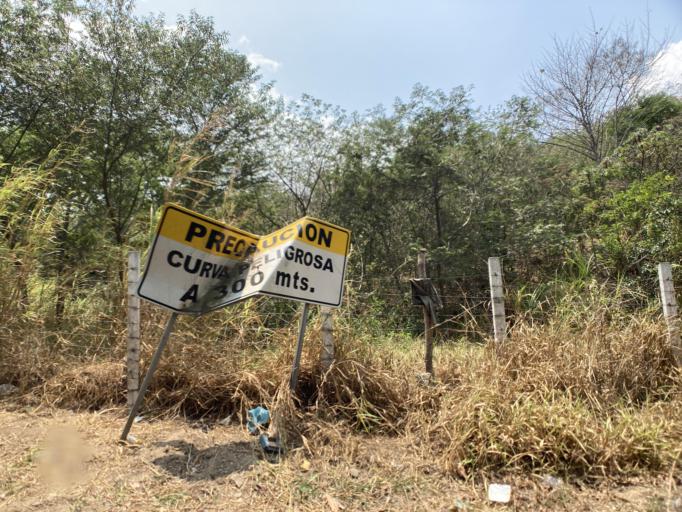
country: GT
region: Santa Rosa
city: Pueblo Nuevo Vinas
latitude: 14.3179
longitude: -90.5317
